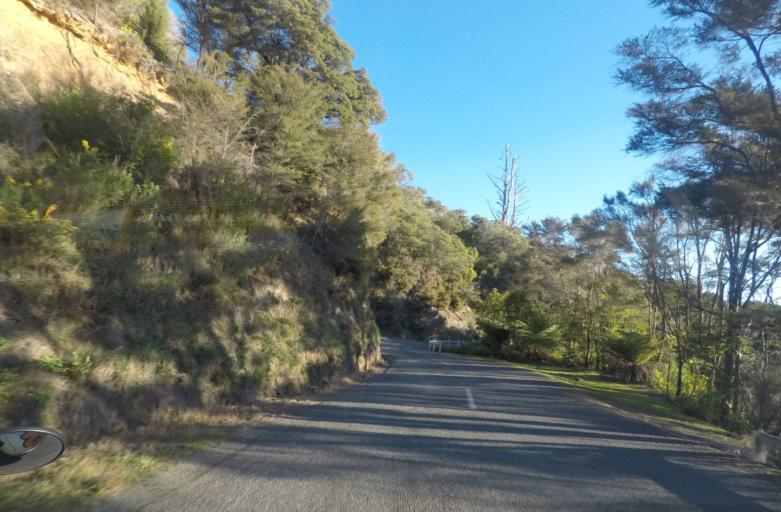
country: NZ
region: Marlborough
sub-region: Marlborough District
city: Picton
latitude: -41.2685
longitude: 173.9556
